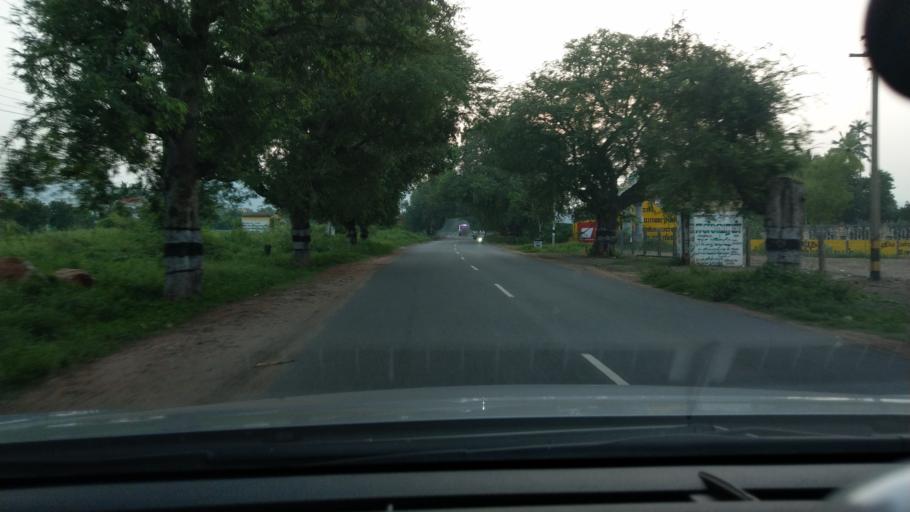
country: IN
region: Tamil Nadu
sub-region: Salem
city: Attur
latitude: 11.5974
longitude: 78.5734
